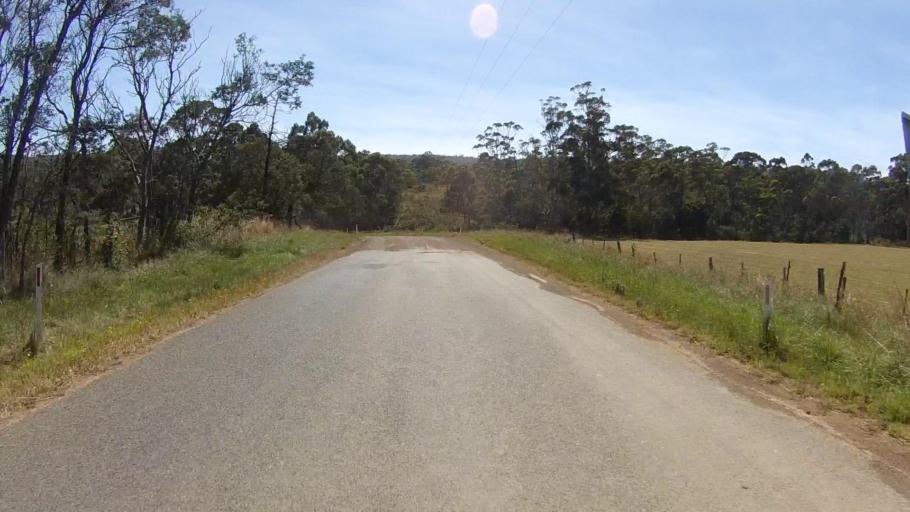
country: AU
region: Tasmania
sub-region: Sorell
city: Sorell
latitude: -42.7488
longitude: 147.7189
